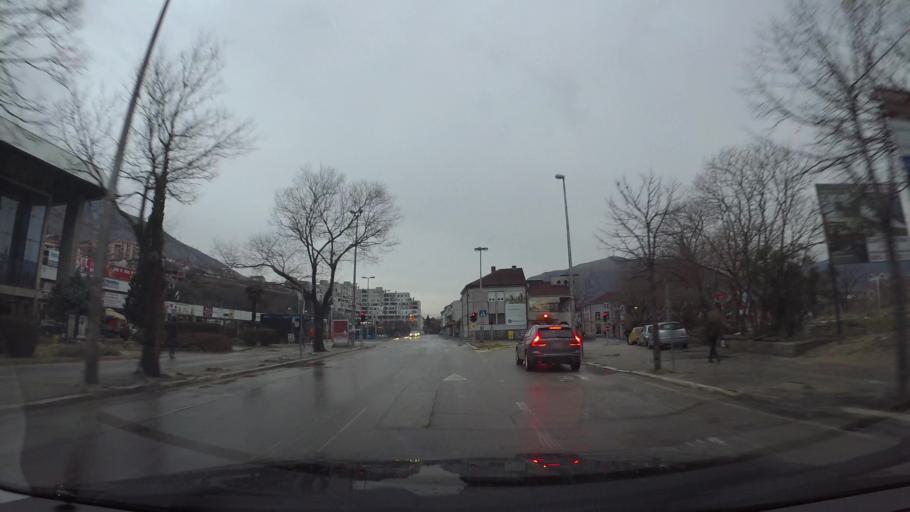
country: BA
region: Federation of Bosnia and Herzegovina
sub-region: Hercegovacko-Bosanski Kanton
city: Mostar
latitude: 43.3489
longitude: 17.8127
